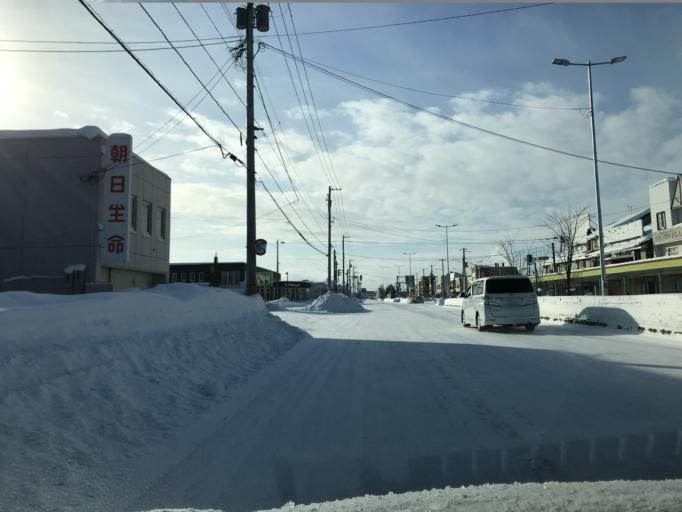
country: JP
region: Hokkaido
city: Nayoro
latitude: 44.3502
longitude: 142.4639
